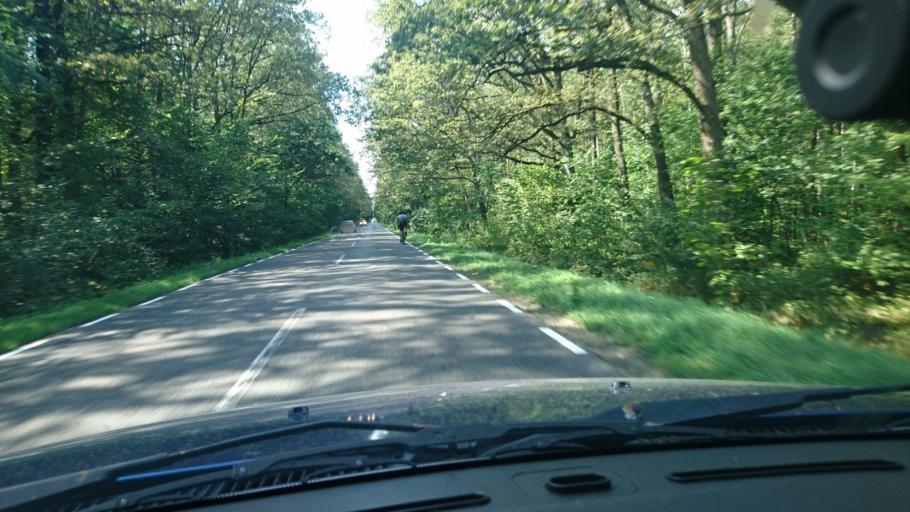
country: PL
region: Greater Poland Voivodeship
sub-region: Powiat ostrowski
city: Odolanow
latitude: 51.5966
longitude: 17.6120
